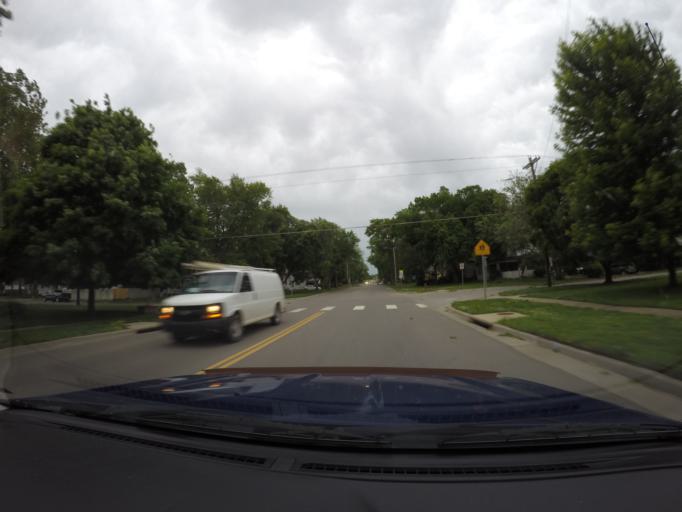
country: US
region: Kansas
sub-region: Clay County
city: Clay Center
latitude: 39.3804
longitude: -97.1287
